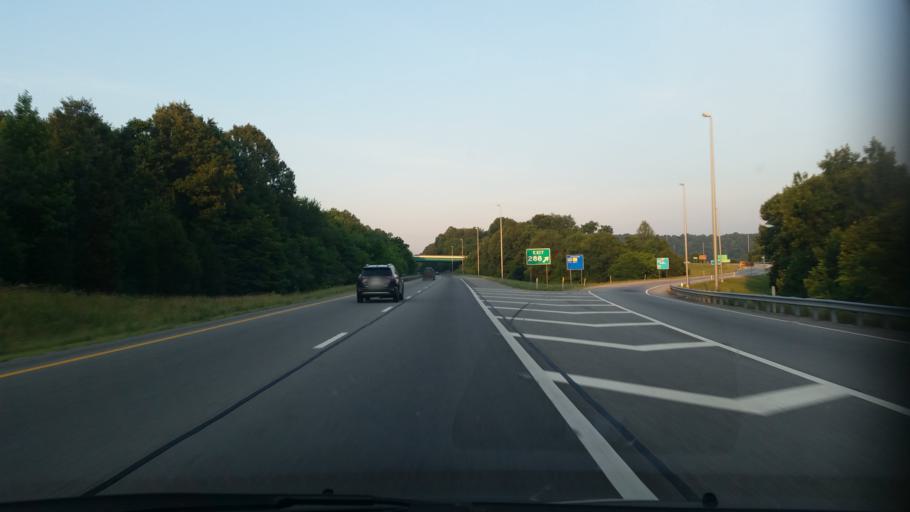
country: US
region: Tennessee
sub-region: Putnam County
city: Cookeville
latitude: 36.1348
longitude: -85.4842
